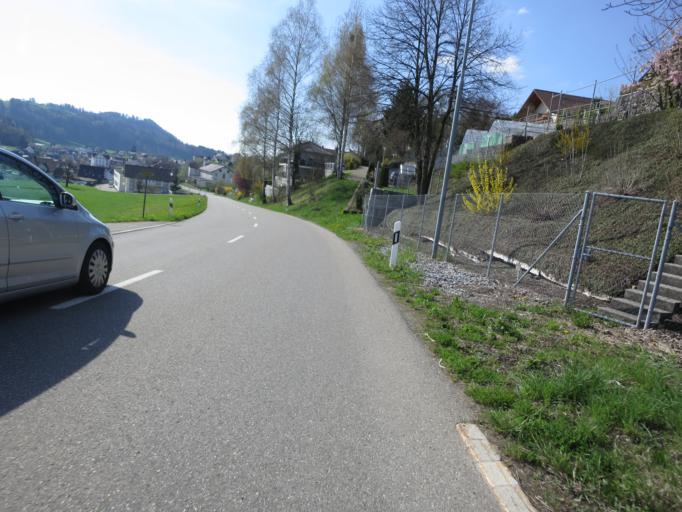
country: CH
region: Zurich
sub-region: Bezirk Hinwil
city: Wald
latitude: 47.2662
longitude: 8.9366
